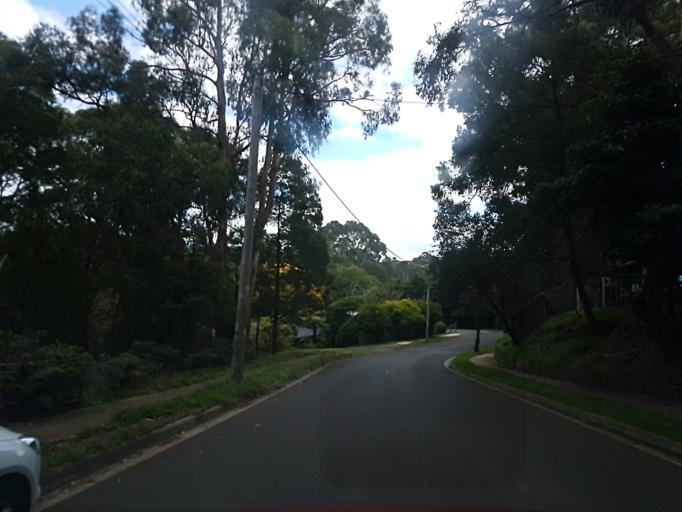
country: AU
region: Victoria
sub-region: Yarra Ranges
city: Tremont
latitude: -37.9009
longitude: 145.3350
